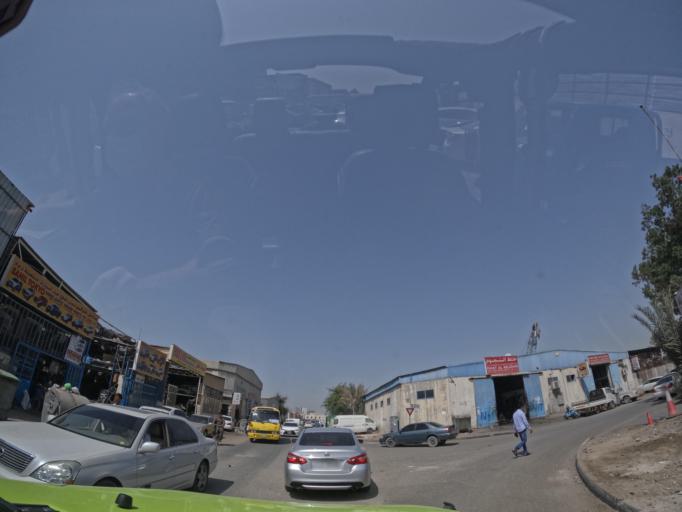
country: AE
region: Ash Shariqah
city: Sharjah
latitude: 25.3155
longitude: 55.4147
